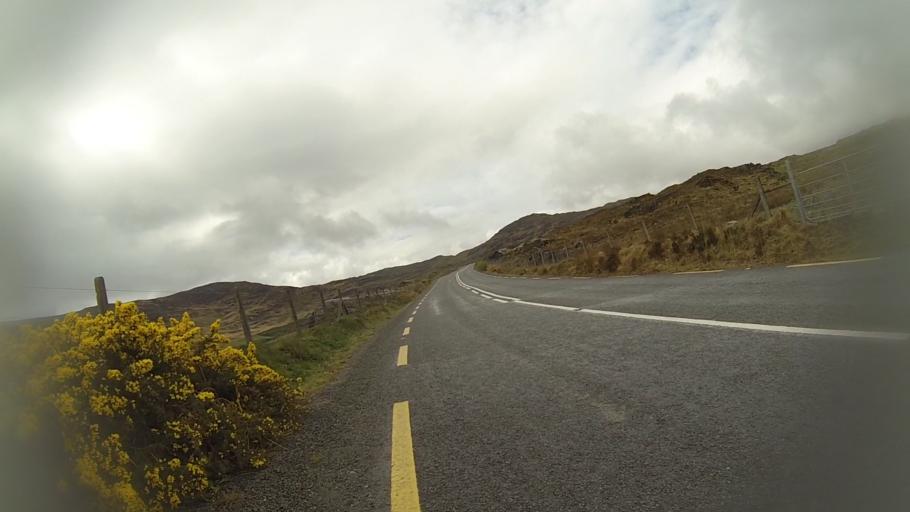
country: IE
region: Munster
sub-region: Ciarrai
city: Kenmare
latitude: 51.7995
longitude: -9.5774
